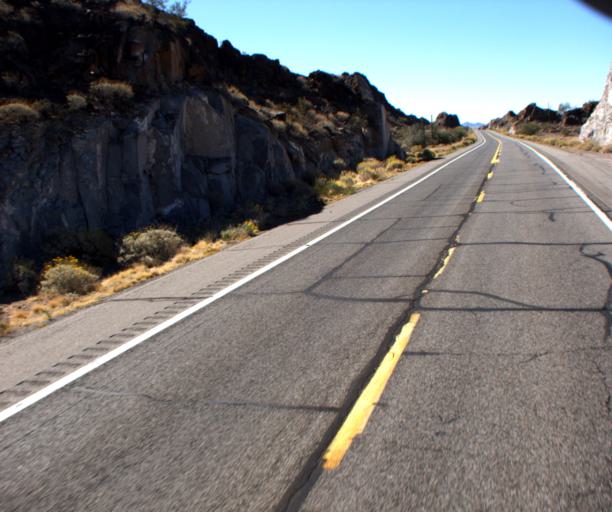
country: US
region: Arizona
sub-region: Pima County
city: Ajo
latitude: 32.5509
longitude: -112.8799
